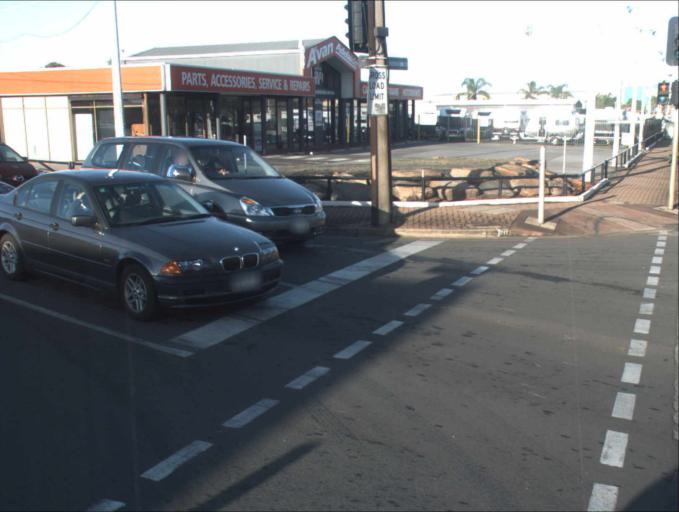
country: AU
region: South Australia
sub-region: Port Adelaide Enfield
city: Gilles Plains
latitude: -34.8604
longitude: 138.6515
